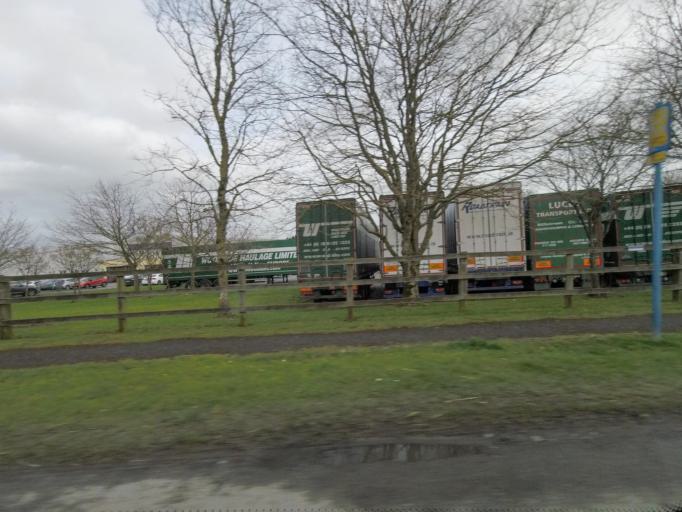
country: IE
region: Leinster
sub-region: Kildare
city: Kilcullen
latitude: 53.1373
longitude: -6.7387
